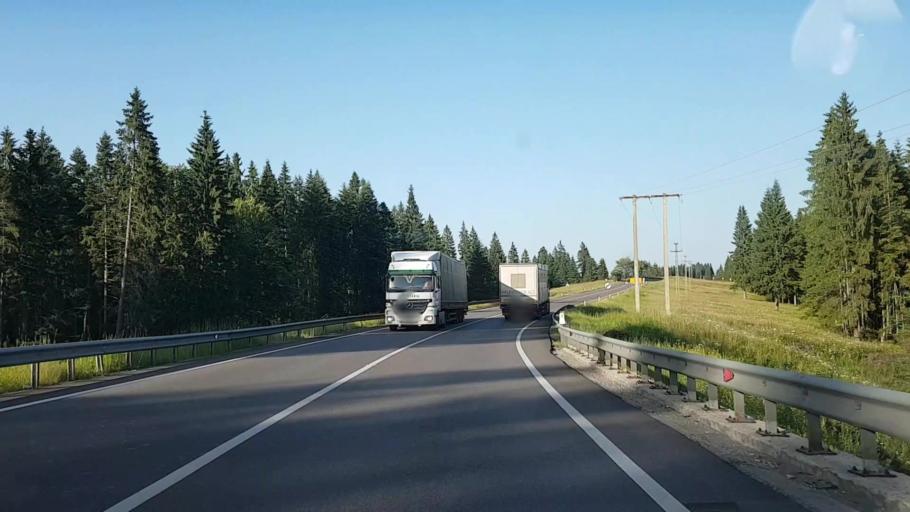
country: RO
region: Suceava
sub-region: Comuna Poiana Stampei
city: Poiana Stampei
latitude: 47.2851
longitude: 25.0552
